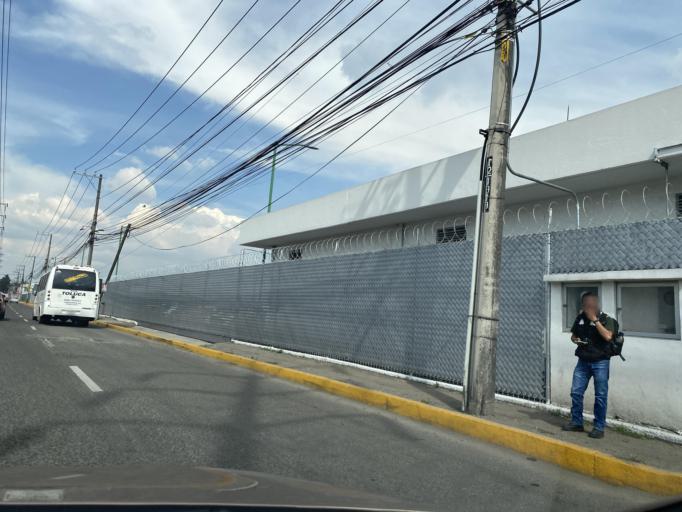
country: IN
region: Karnataka
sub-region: Dakshina Kannada
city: Puttur
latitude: 12.7347
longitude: 75.1841
